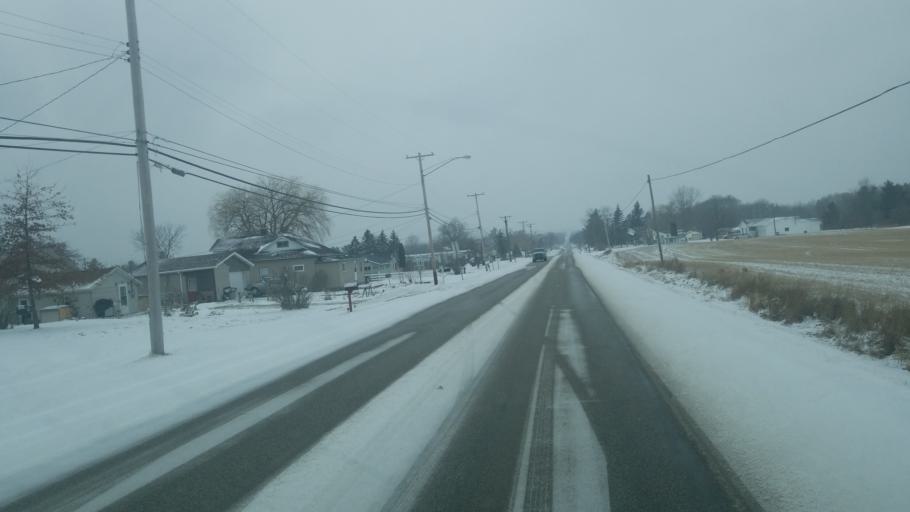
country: US
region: Michigan
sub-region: Osceola County
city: Evart
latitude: 44.1025
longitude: -85.1344
